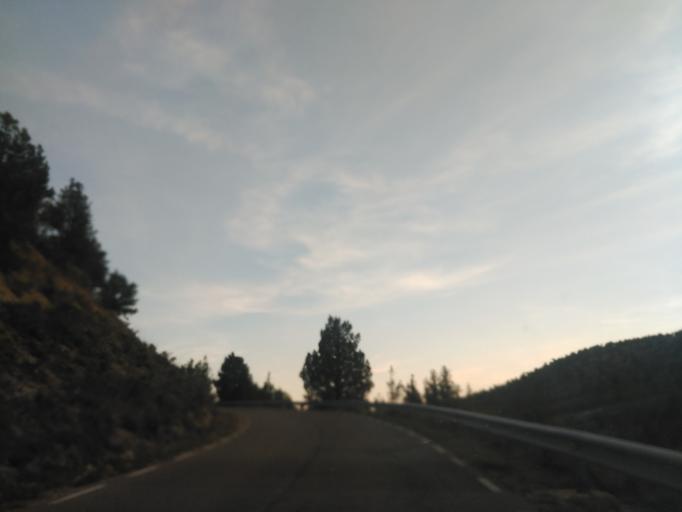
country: ES
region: Castille and Leon
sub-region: Provincia de Soria
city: Ucero
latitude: 41.7299
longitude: -3.0455
